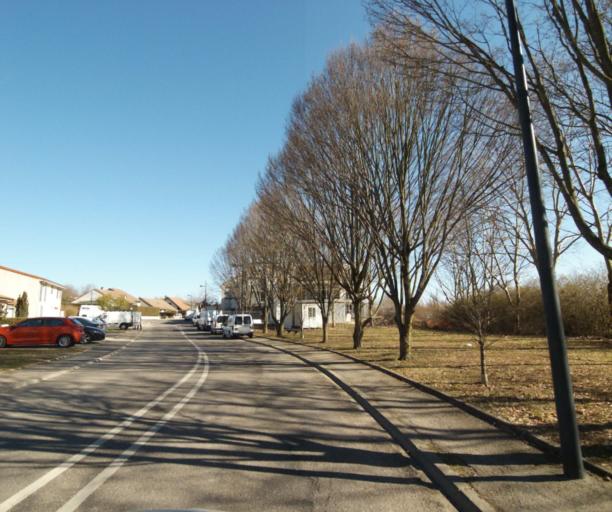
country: FR
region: Lorraine
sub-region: Departement de Meurthe-et-Moselle
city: Ludres
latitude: 48.6232
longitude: 6.1732
